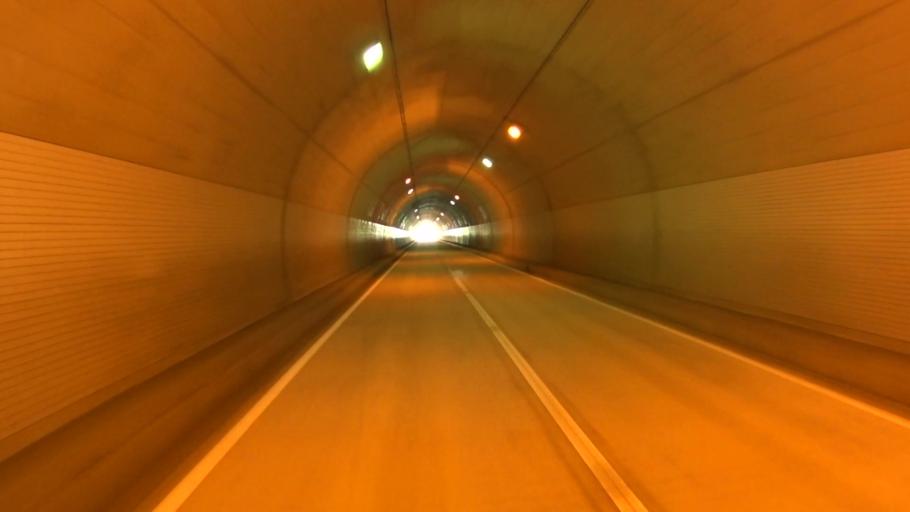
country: JP
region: Kyoto
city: Kameoka
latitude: 35.1130
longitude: 135.5639
